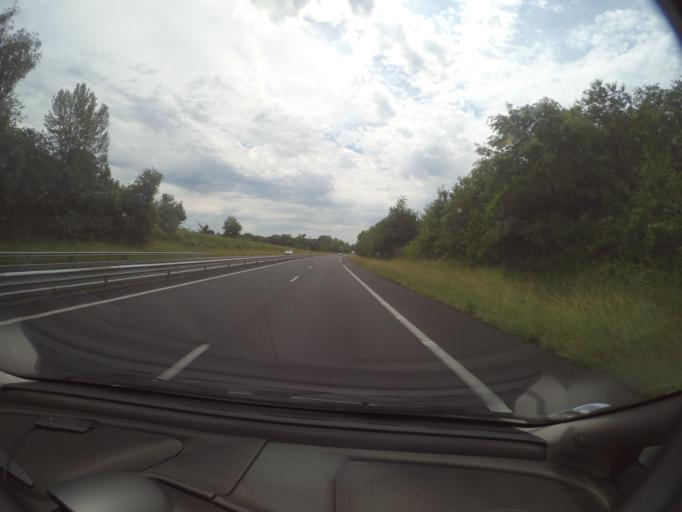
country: FR
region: Pays de la Loire
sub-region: Departement de Maine-et-Loire
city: Seiches-sur-le-Loir
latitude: 47.5603
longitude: -0.3308
